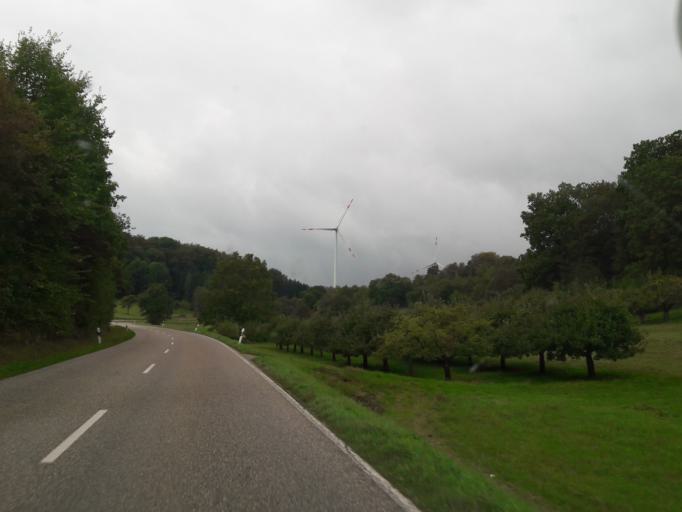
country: DE
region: Baden-Wuerttemberg
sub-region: Regierungsbezirk Stuttgart
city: Widdern
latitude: 49.3064
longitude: 9.4214
